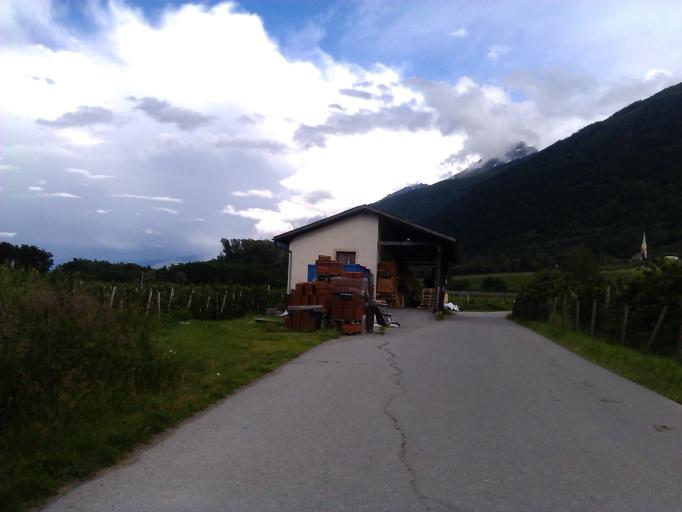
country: IT
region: Trentino-Alto Adige
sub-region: Bolzano
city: Prato Allo Stelvio
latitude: 46.6196
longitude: 10.6277
